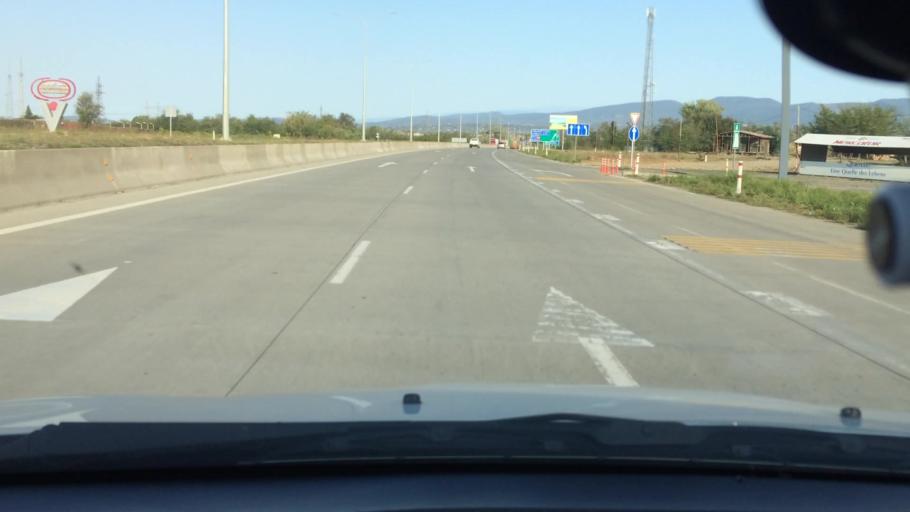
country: GE
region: Imereti
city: Zestap'oni
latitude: 42.1487
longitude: 42.9627
